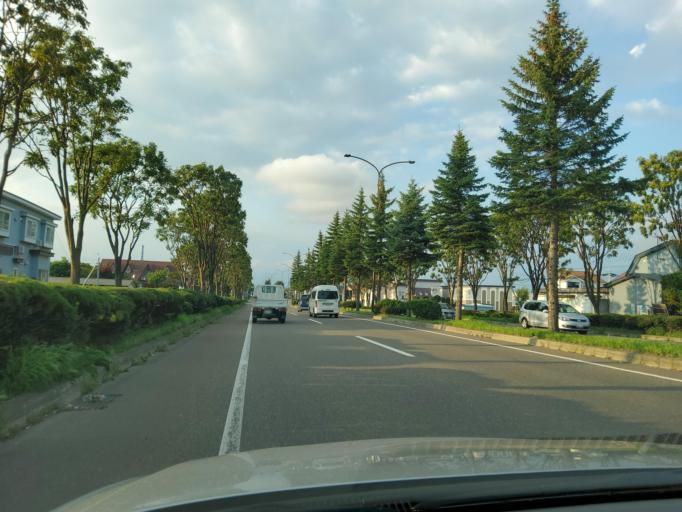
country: JP
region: Hokkaido
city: Obihiro
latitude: 42.9322
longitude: 143.1629
